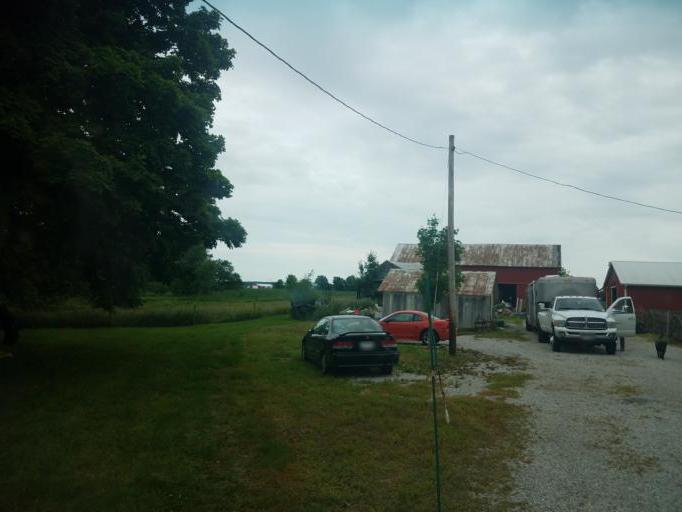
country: US
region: Ohio
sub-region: Union County
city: Richwood
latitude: 40.6197
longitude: -83.3428
